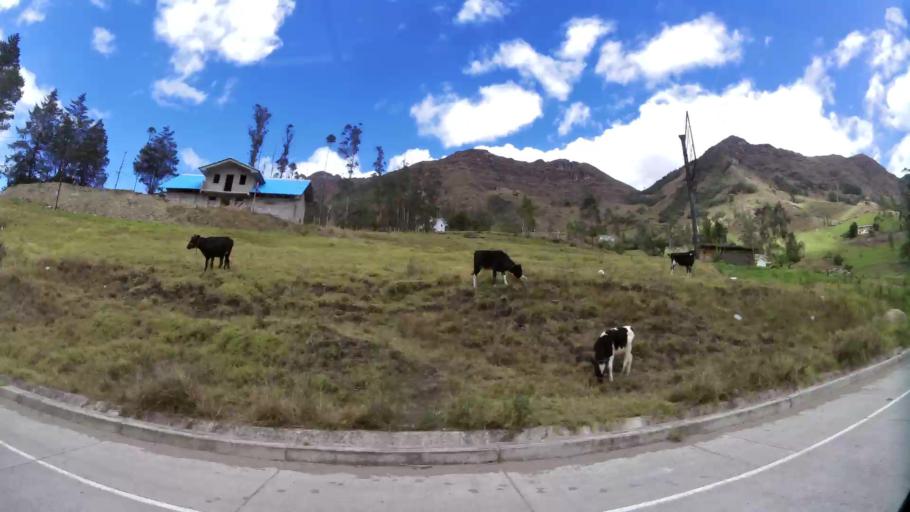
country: EC
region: Azuay
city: Cuenca
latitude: -3.1410
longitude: -79.1399
